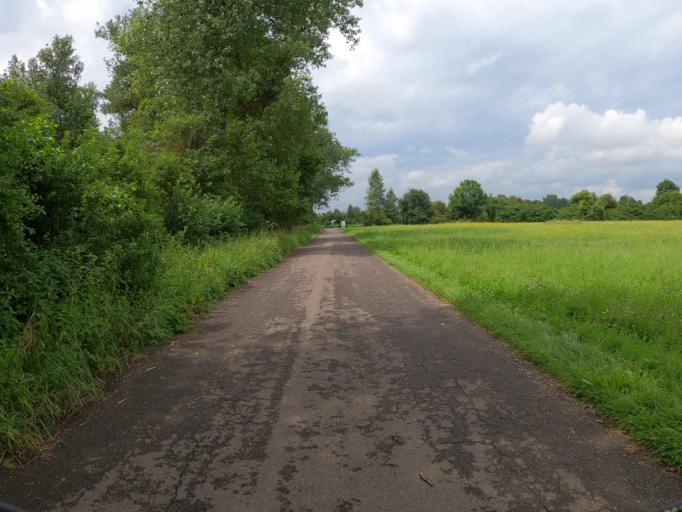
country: DE
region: Baden-Wuerttemberg
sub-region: Tuebingen Region
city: Langenau
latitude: 48.4847
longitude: 10.1521
